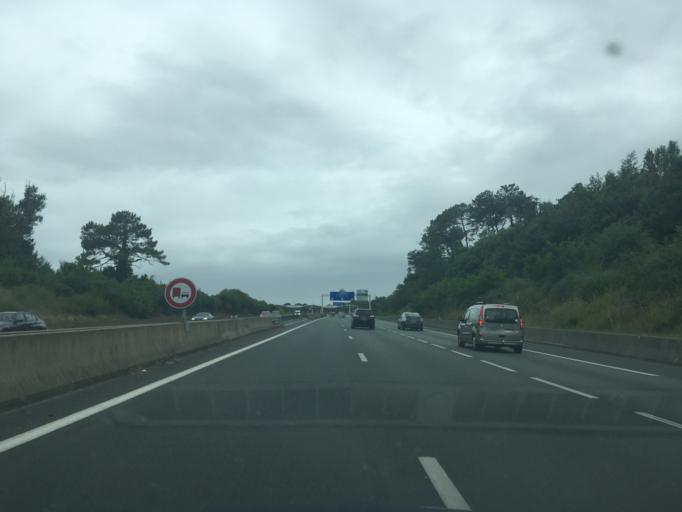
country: FR
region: Aquitaine
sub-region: Departement des Pyrenees-Atlantiques
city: Arbonne
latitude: 43.4475
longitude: -1.5457
